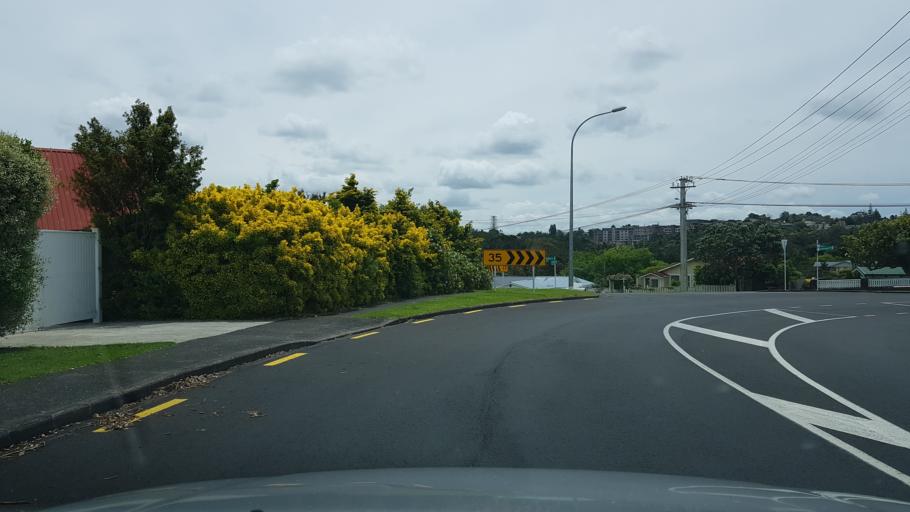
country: NZ
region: Auckland
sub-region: Auckland
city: North Shore
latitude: -36.8155
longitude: 174.7070
